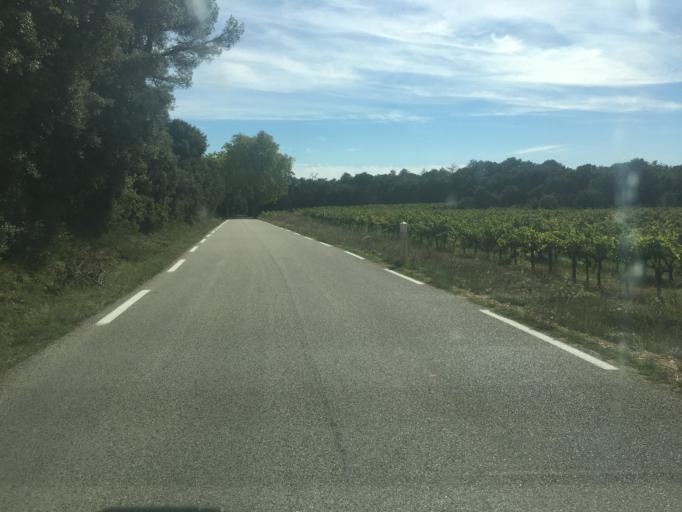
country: FR
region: Languedoc-Roussillon
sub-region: Departement du Gard
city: Connaux
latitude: 44.0483
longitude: 4.5675
